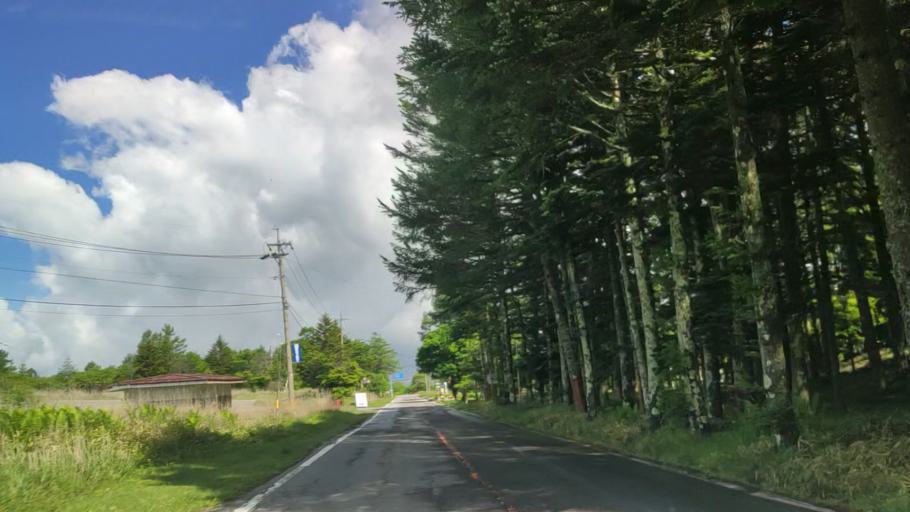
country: JP
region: Nagano
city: Suwa
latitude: 36.0985
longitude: 138.1597
